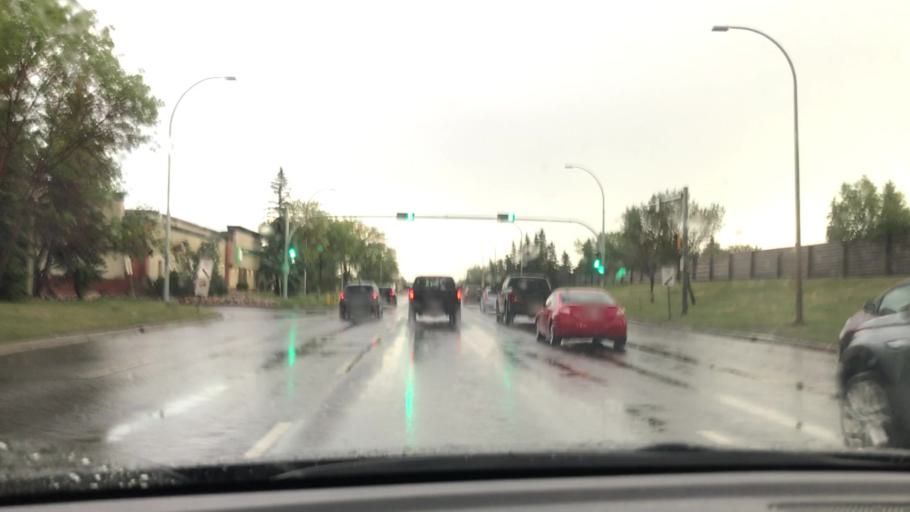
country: CA
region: Alberta
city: Edmonton
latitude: 53.4725
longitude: -113.4957
